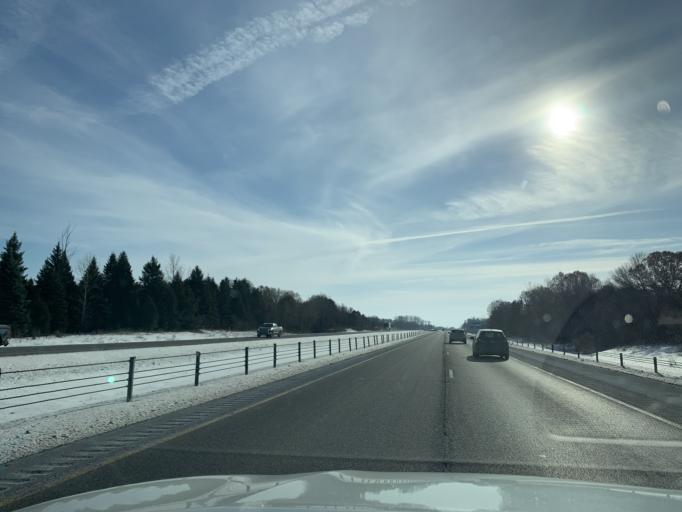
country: US
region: Minnesota
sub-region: Chisago County
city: Wyoming
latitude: 45.3091
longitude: -93.0034
